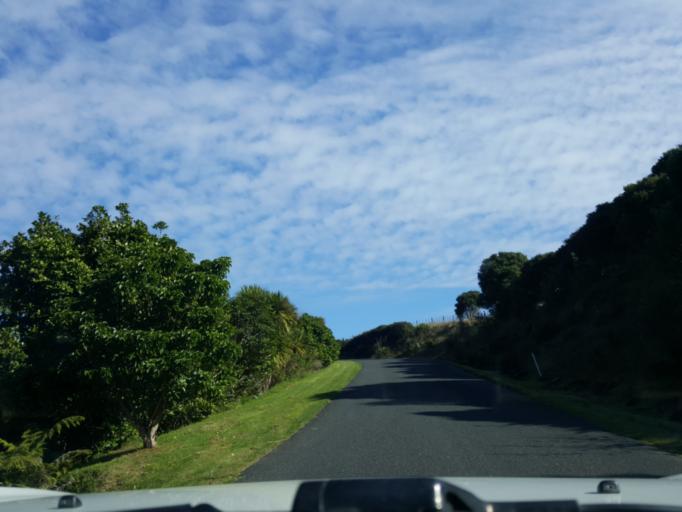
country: NZ
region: Waikato
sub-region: Waikato District
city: Raglan
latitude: -37.8183
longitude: 174.8342
